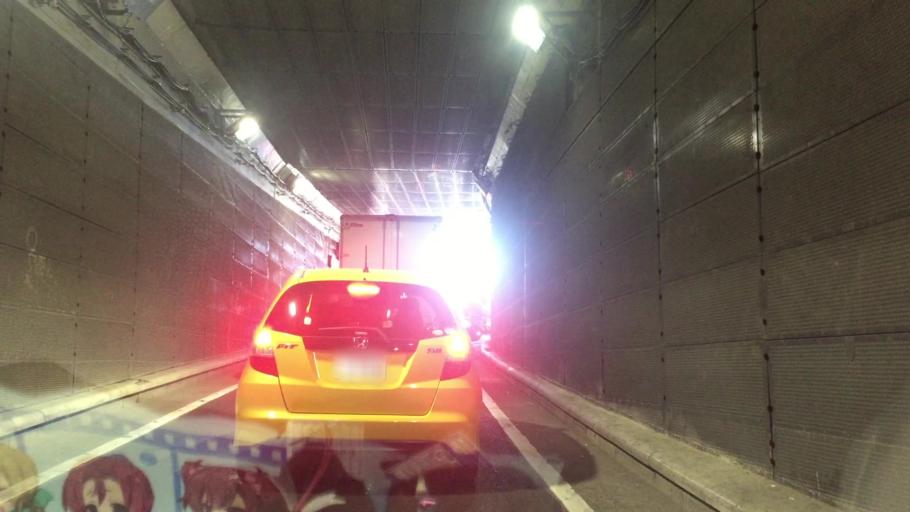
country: JP
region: Kanagawa
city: Yokohama
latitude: 35.4708
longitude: 139.6082
